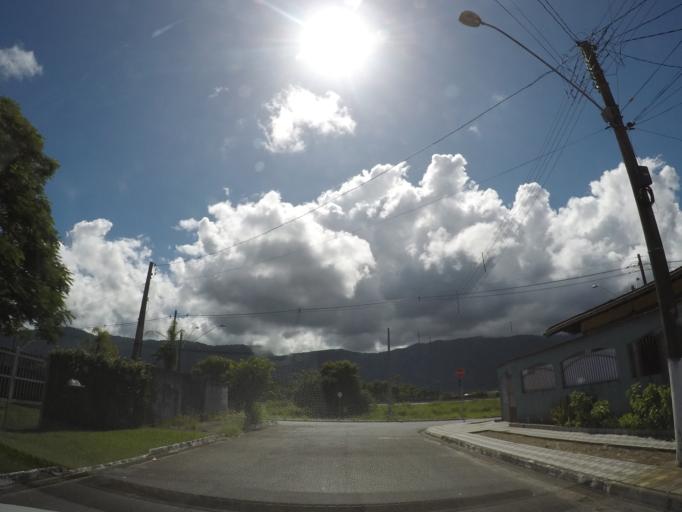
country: BR
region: Sao Paulo
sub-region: Mongagua
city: Mongagua
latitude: -24.0657
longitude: -46.5679
